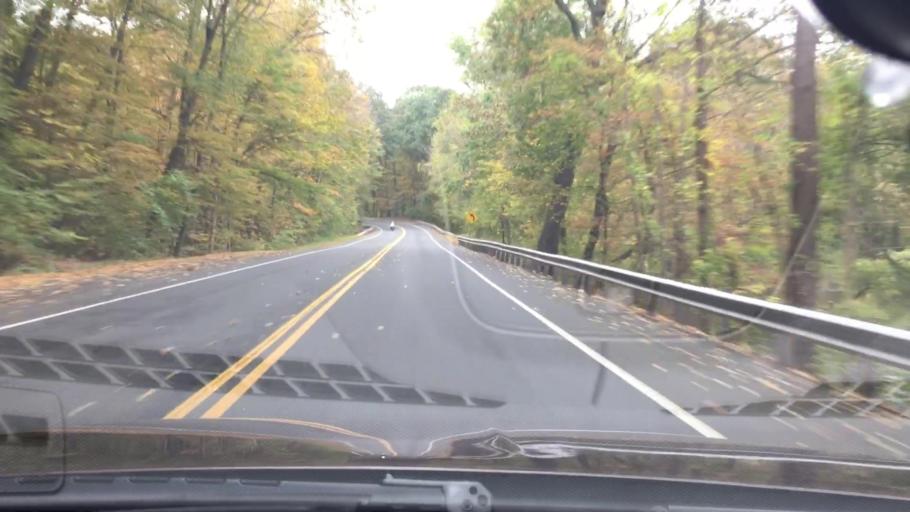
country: US
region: Connecticut
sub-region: Hartford County
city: Broad Brook
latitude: 41.9121
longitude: -72.5590
